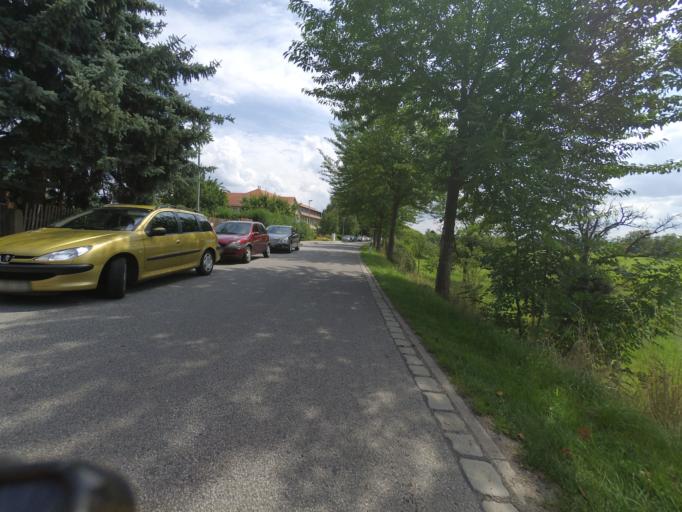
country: DE
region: Saxony
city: Heidenau
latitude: 51.0060
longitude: 13.8749
